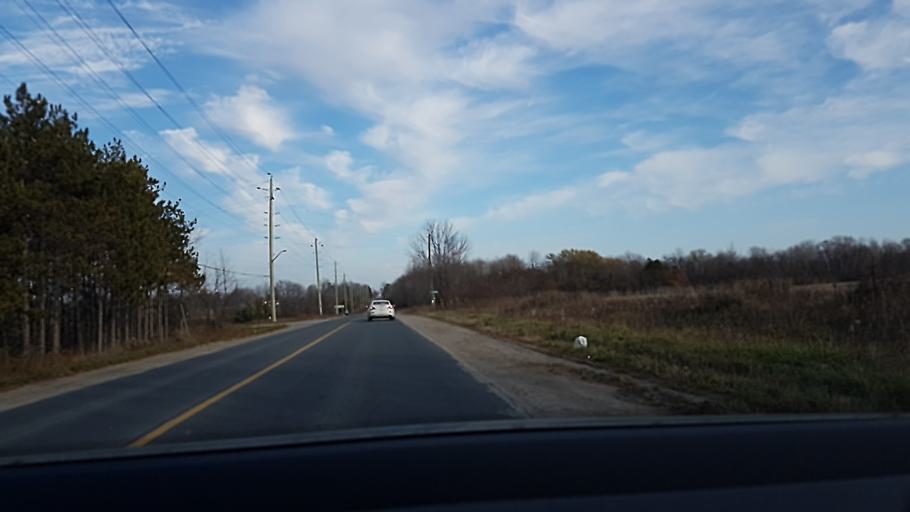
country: CA
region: Ontario
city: Barrie
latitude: 44.3721
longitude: -79.5806
